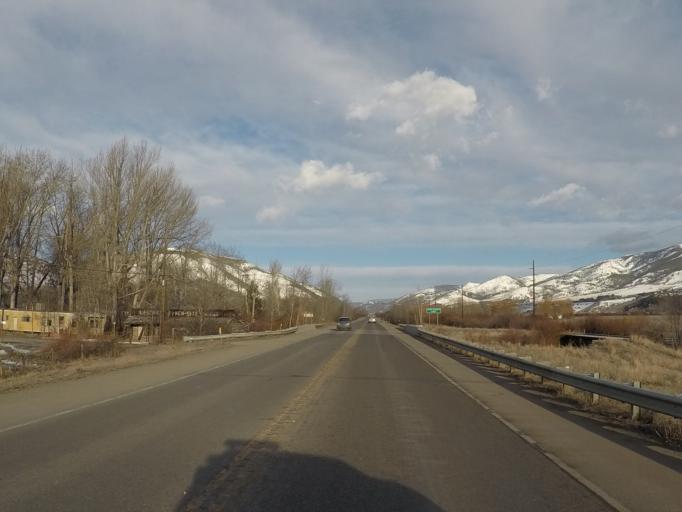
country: US
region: Montana
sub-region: Deer Lodge County
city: Anaconda
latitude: 46.1421
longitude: -112.9912
